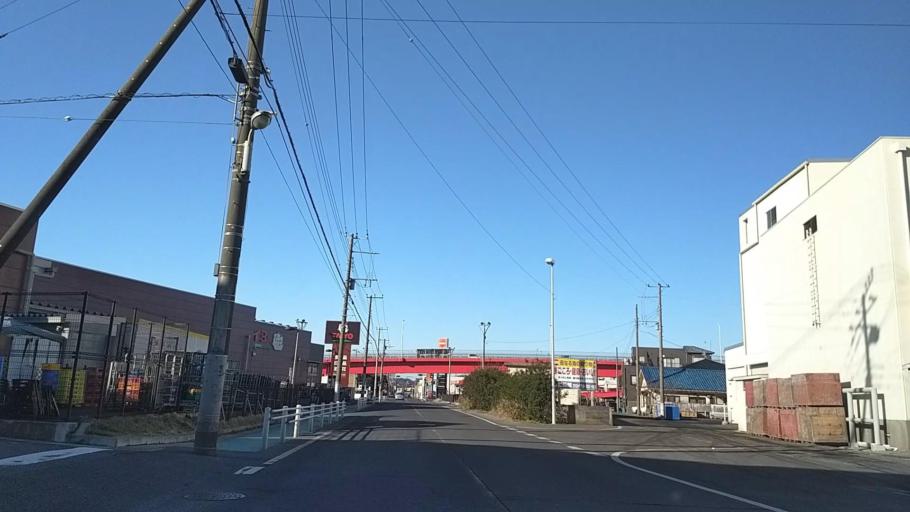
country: JP
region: Chiba
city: Hasaki
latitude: 35.7351
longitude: 140.8253
